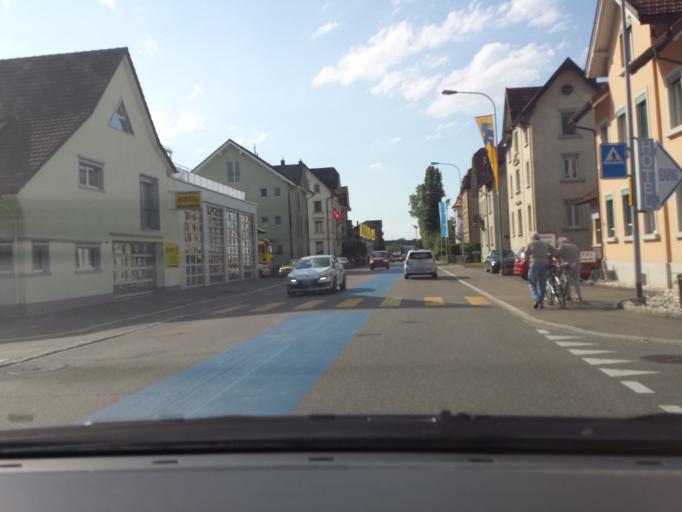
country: CH
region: Thurgau
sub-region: Arbon District
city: Arbon
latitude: 47.5036
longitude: 9.4377
